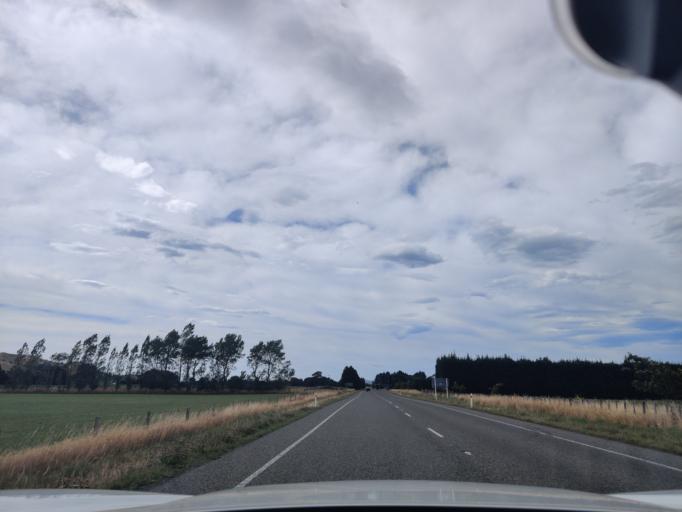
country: NZ
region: Wellington
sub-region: Masterton District
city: Masterton
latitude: -40.8555
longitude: 175.6388
